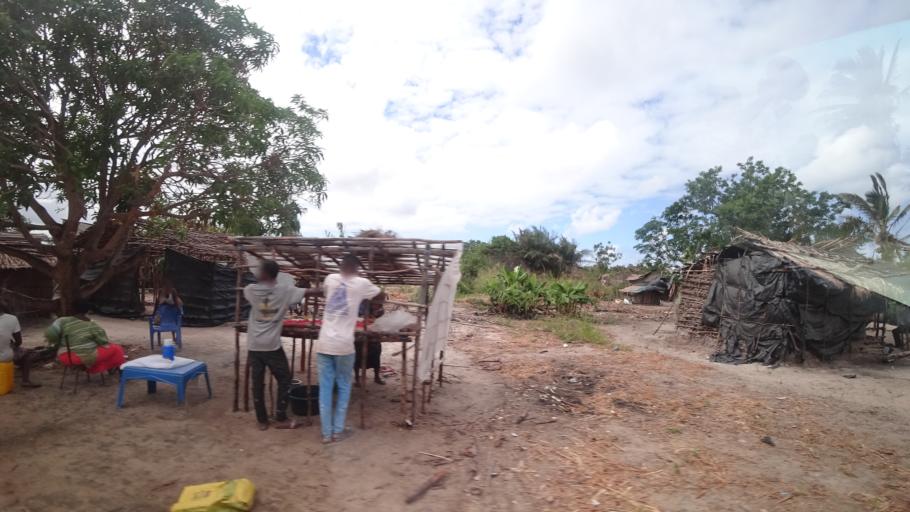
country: MZ
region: Sofala
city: Beira
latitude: -19.6146
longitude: 35.2159
